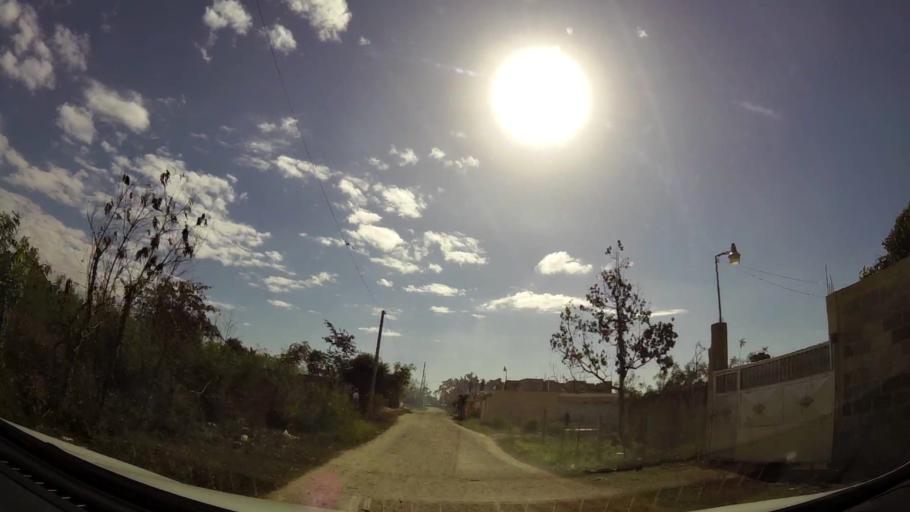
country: DO
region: Santo Domingo
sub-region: Santo Domingo
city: Boca Chica
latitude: 18.4645
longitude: -69.6048
